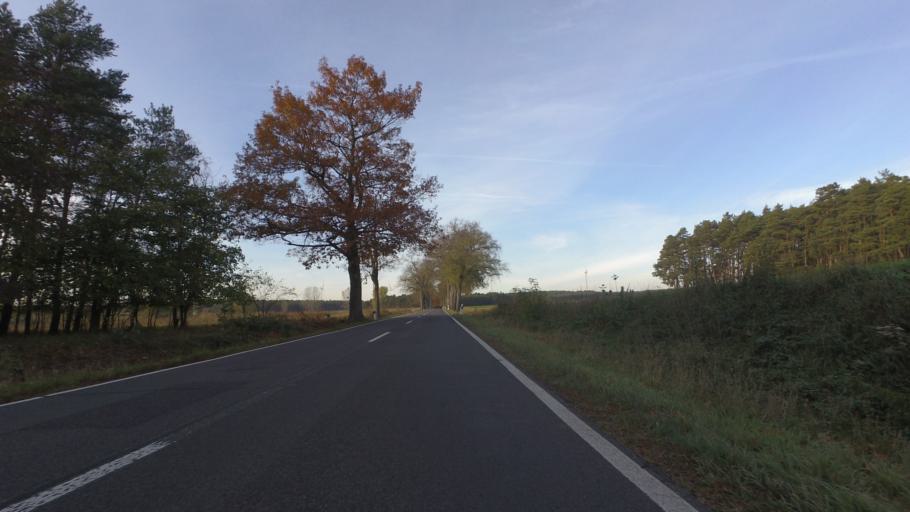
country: DE
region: Brandenburg
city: Sperenberg
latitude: 52.1953
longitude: 13.3159
